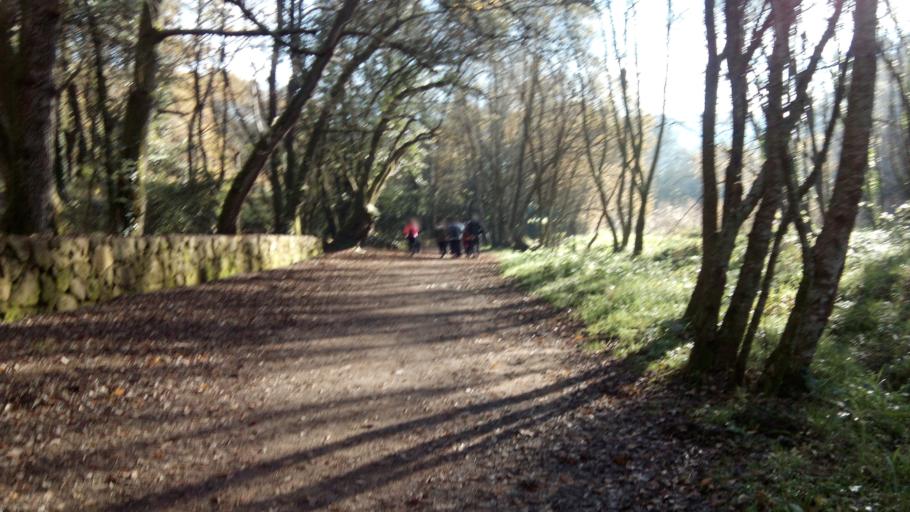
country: ES
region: Galicia
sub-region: Provincia de Pontevedra
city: Meis
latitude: 42.4843
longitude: -8.7435
